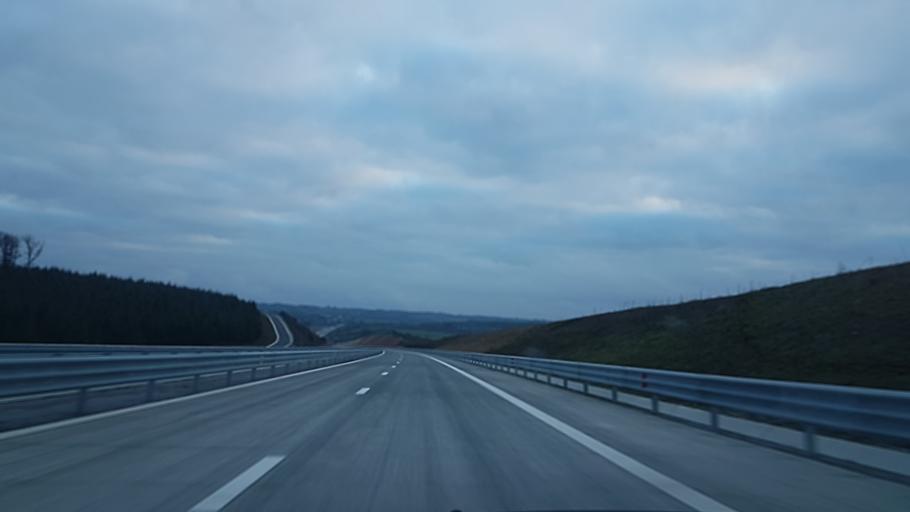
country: FR
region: Champagne-Ardenne
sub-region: Departement des Ardennes
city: Rocroi
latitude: 49.9874
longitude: 4.5406
